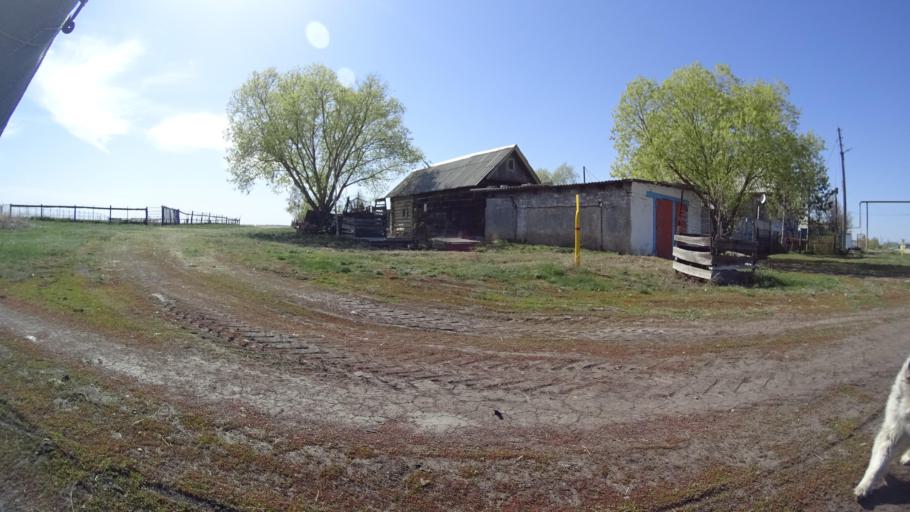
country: RU
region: Chelyabinsk
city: Chesma
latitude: 53.7877
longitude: 61.0393
